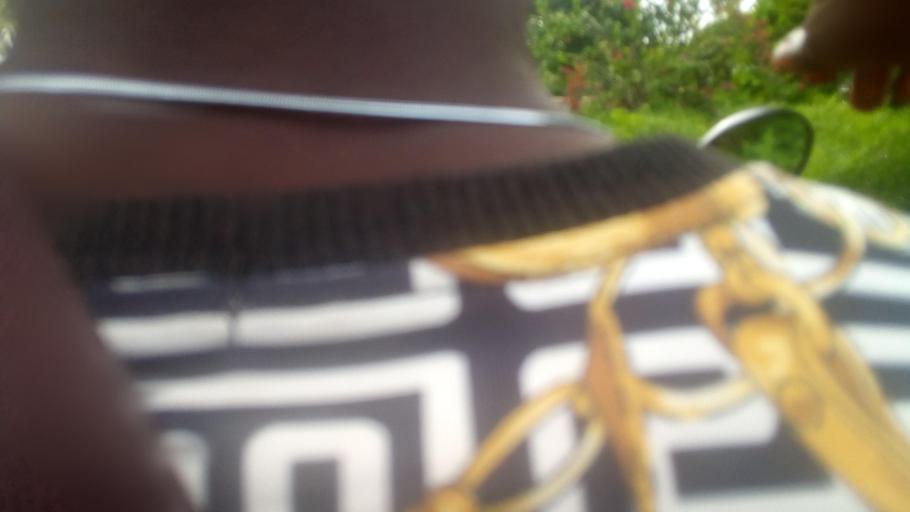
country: SL
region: Eastern Province
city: Pendembu
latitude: 8.1003
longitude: -10.6931
